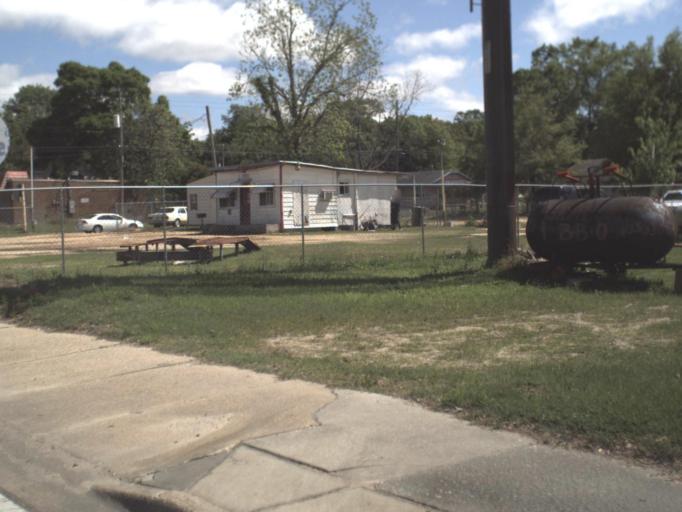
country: US
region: Florida
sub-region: Escambia County
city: Goulding
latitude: 30.4334
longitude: -87.2404
